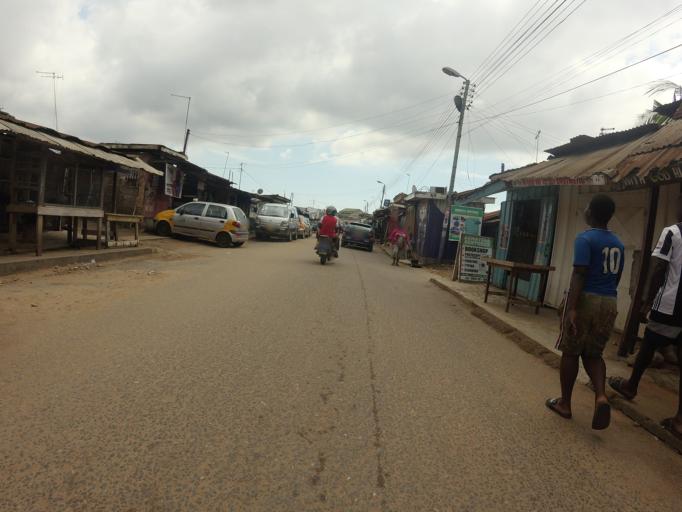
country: GH
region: Greater Accra
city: Accra
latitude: 5.5892
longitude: -0.2015
